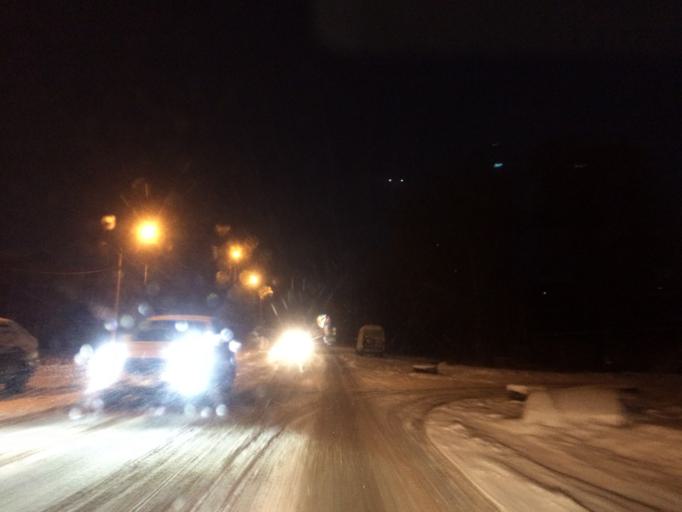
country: RU
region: Tula
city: Mendeleyevskiy
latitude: 54.1573
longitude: 37.6087
